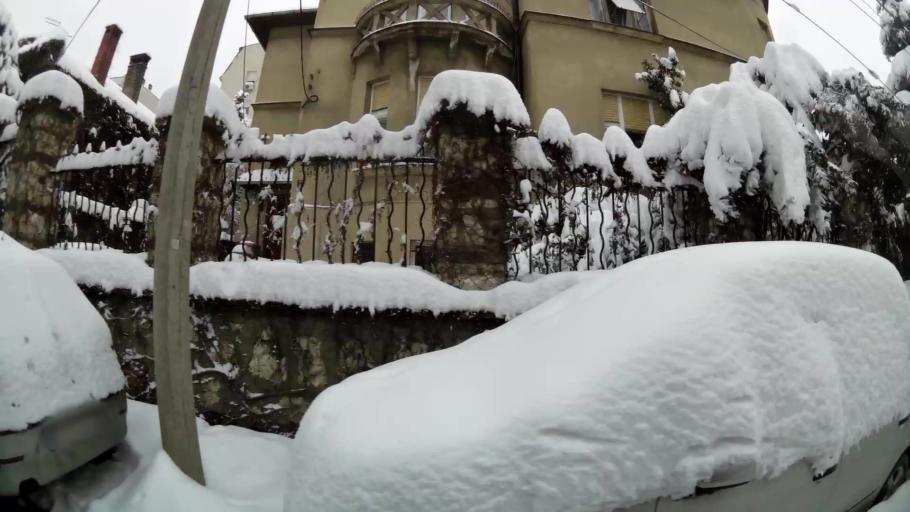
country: RS
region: Central Serbia
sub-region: Belgrade
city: Vracar
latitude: 44.7949
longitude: 20.4702
